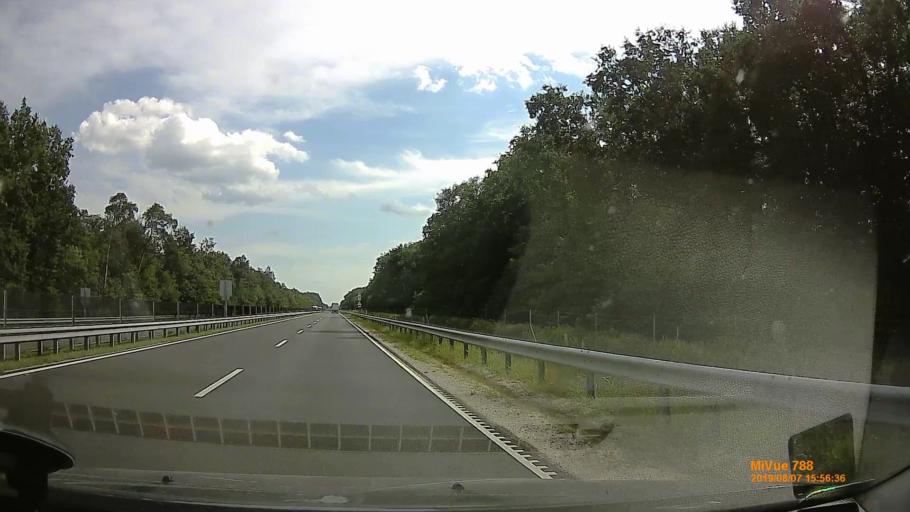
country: HU
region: Vas
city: Kormend
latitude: 47.0579
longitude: 16.6157
